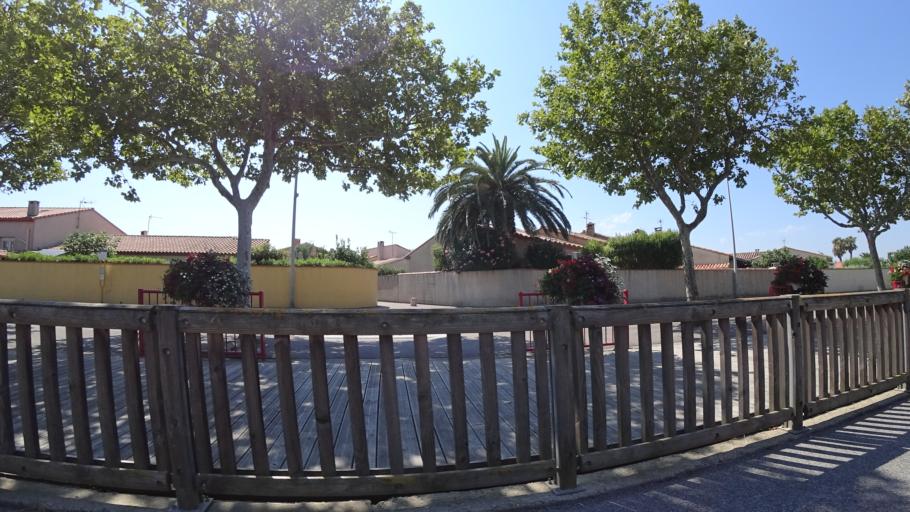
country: FR
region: Languedoc-Roussillon
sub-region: Departement des Pyrenees-Orientales
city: Sainte-Marie-Plage
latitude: 42.7285
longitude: 3.0208
